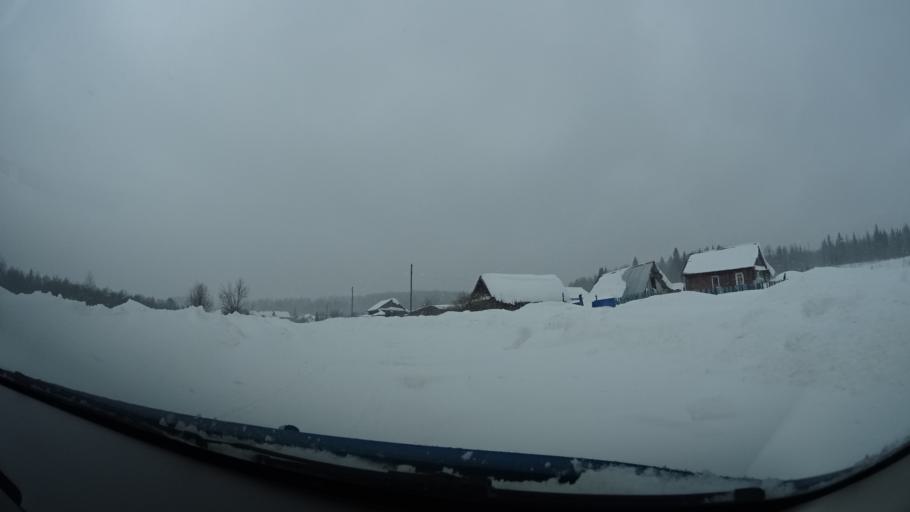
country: RU
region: Perm
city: Kuyeda
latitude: 56.6173
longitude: 55.7102
